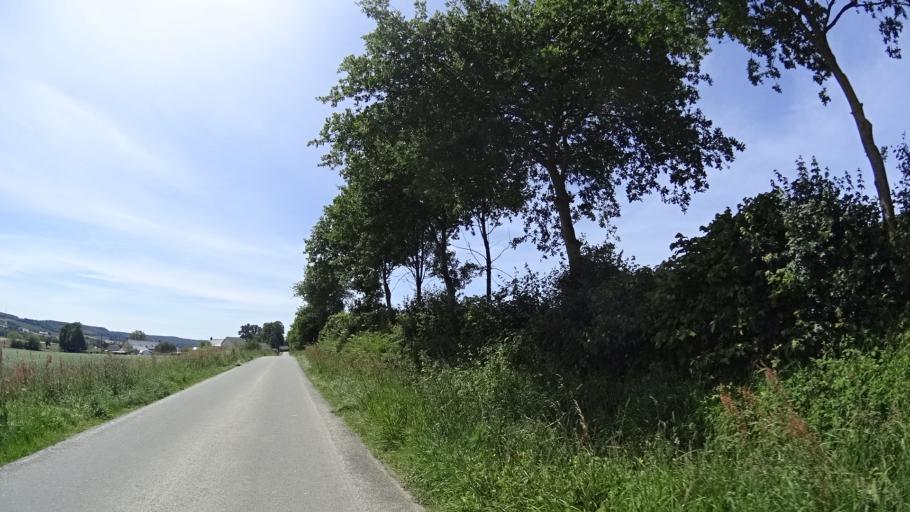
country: FR
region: Brittany
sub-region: Departement d'Ille-et-Vilaine
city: Iffendic
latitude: 48.1478
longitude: -1.9949
